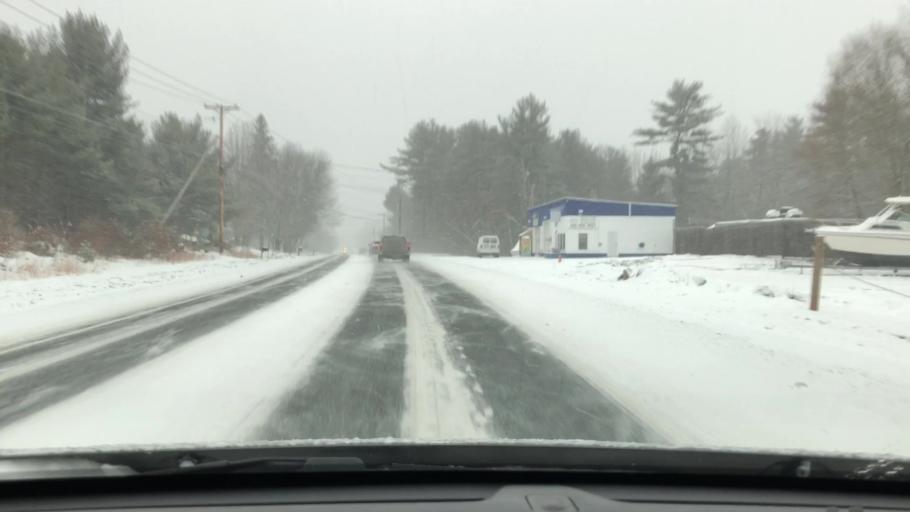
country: US
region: New Hampshire
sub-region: Strafford County
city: Lee
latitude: 43.1833
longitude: -70.9993
